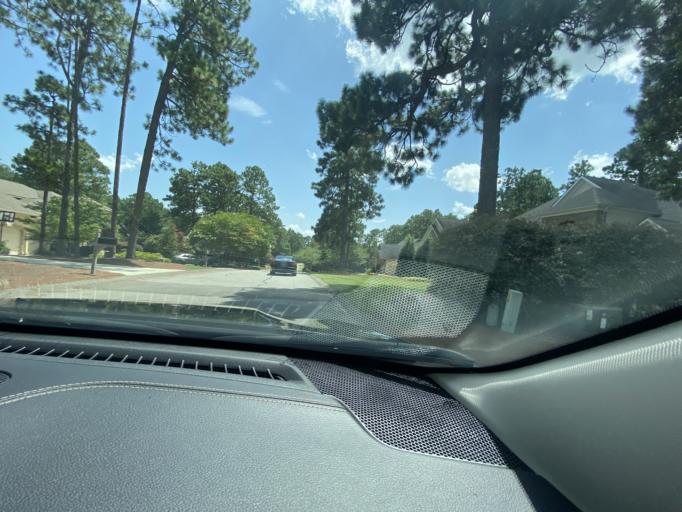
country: US
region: North Carolina
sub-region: Moore County
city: Pinehurst
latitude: 35.1942
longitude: -79.4311
